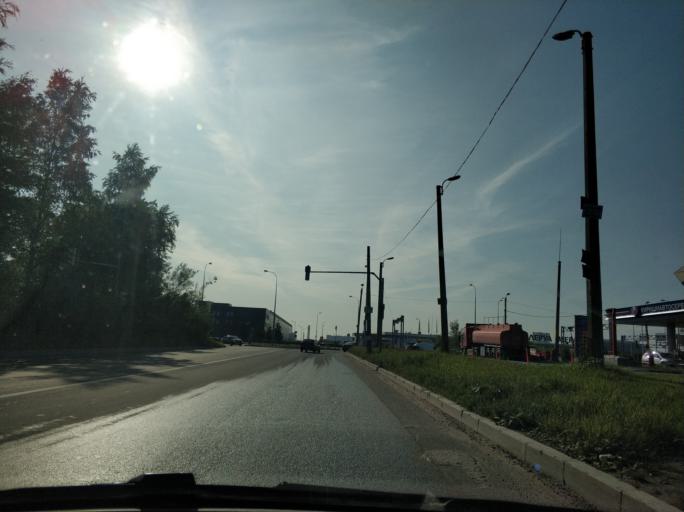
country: RU
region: Leningrad
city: Bugry
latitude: 60.0578
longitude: 30.3842
